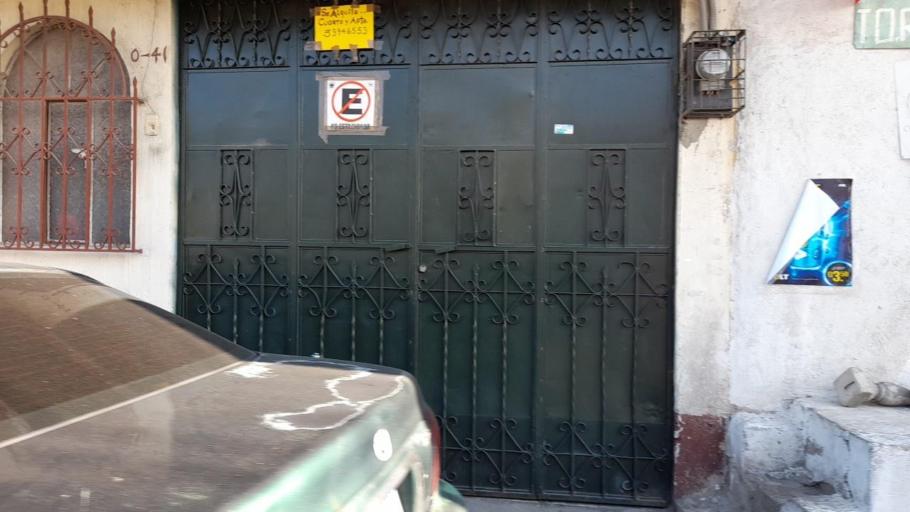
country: GT
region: Quetzaltenango
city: Quetzaltenango
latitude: 14.8395
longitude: -91.5132
